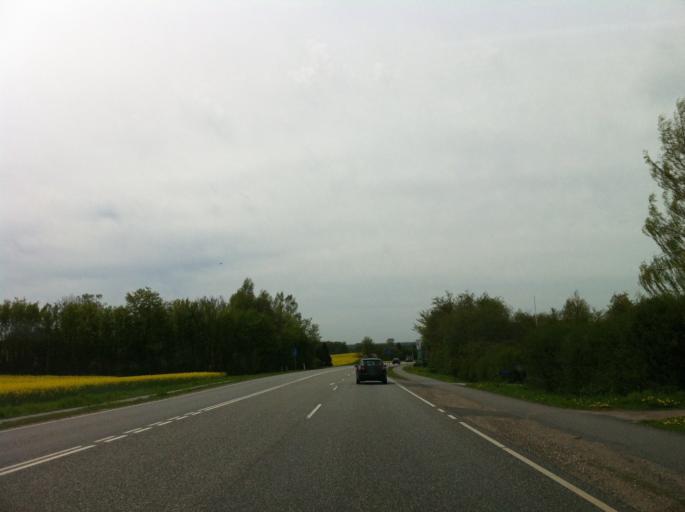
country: DK
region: Zealand
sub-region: Lejre Kommune
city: Kirke Hvalso
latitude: 55.5028
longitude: 11.8819
